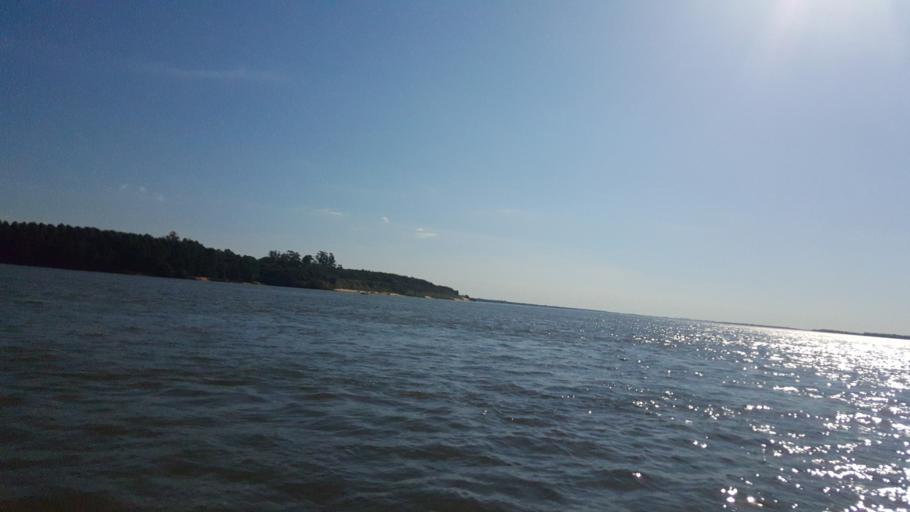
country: AR
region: Corrientes
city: Ituzaingo
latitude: -27.6019
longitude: -56.8568
